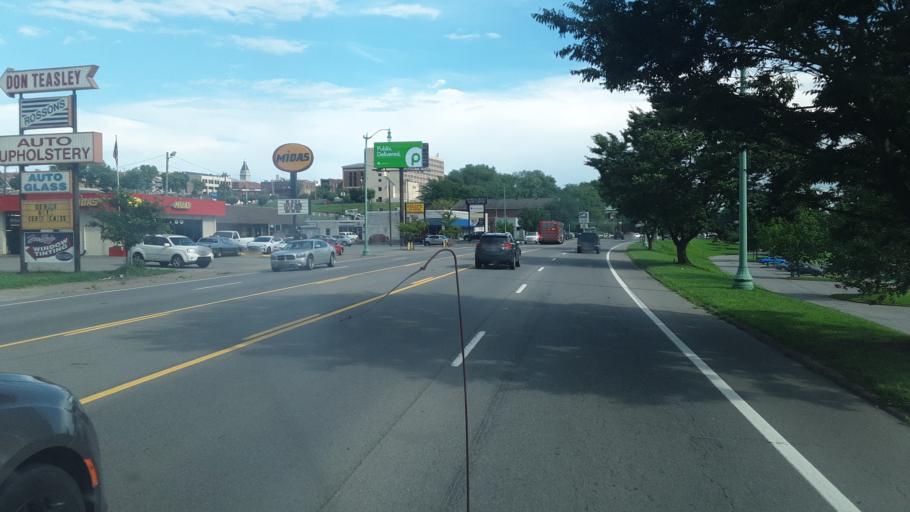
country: US
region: Tennessee
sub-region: Montgomery County
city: Clarksville
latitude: 36.5314
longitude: -87.3647
